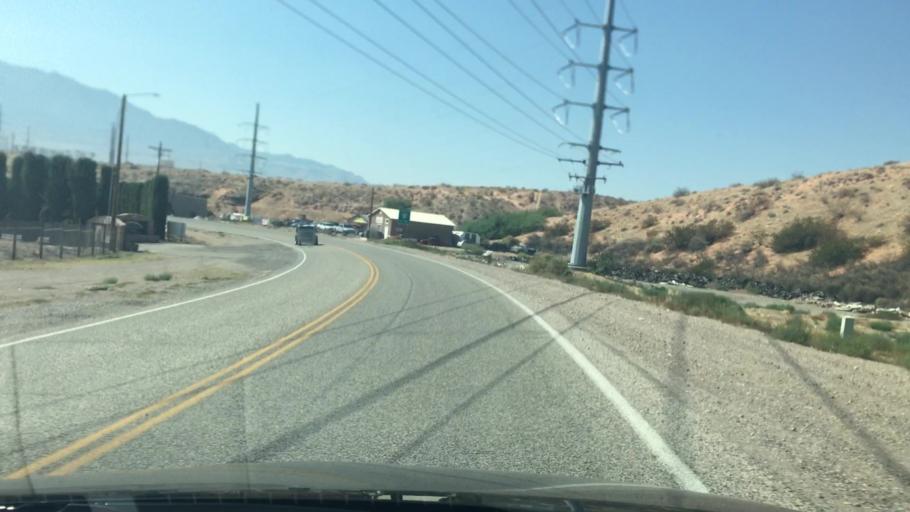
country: US
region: Arizona
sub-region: Mohave County
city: Beaver Dam
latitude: 36.8993
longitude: -113.9347
